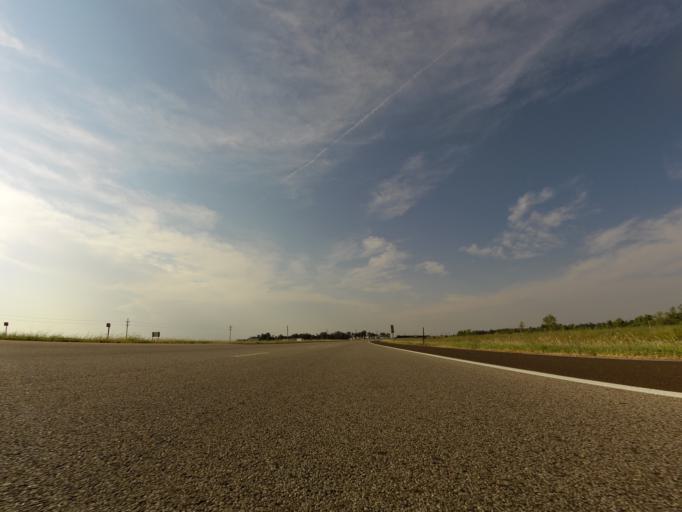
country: US
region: Kansas
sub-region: Reno County
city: South Hutchinson
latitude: 37.9747
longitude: -97.9386
